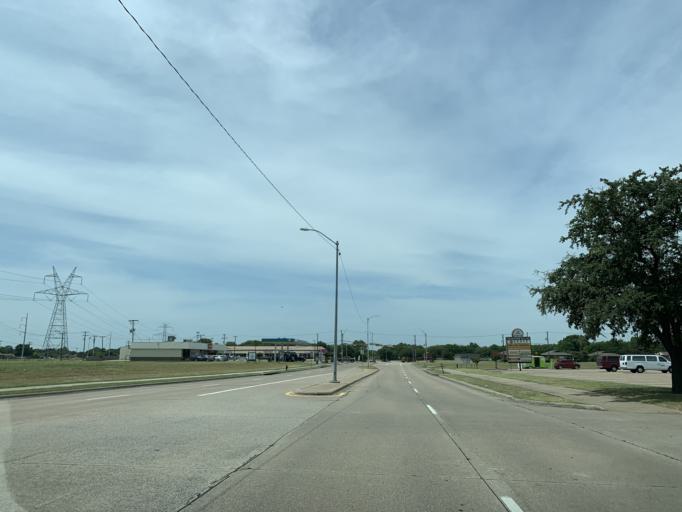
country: US
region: Texas
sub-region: Dallas County
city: Grand Prairie
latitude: 32.6584
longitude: -97.0258
